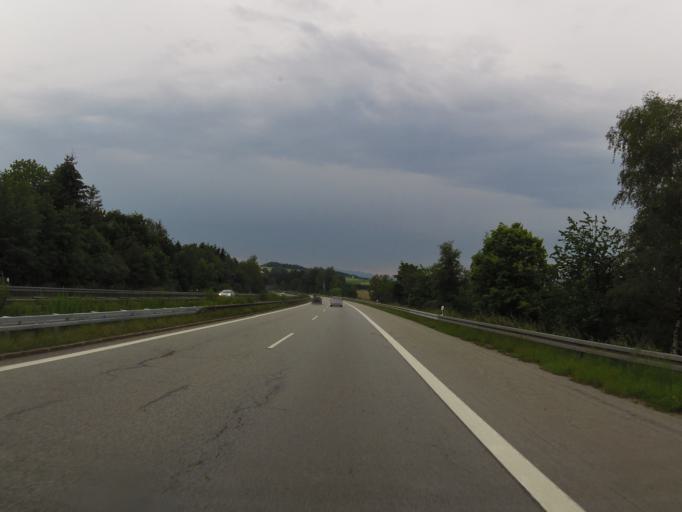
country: DE
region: Bavaria
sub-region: Lower Bavaria
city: Aussernzell
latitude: 48.6981
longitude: 13.1920
